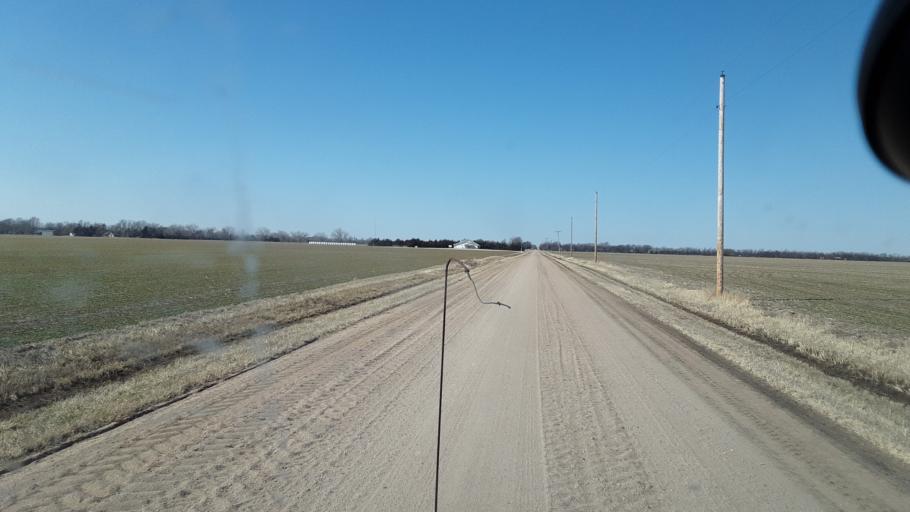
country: US
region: Kansas
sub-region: Reno County
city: South Hutchinson
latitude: 37.9846
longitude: -98.0164
